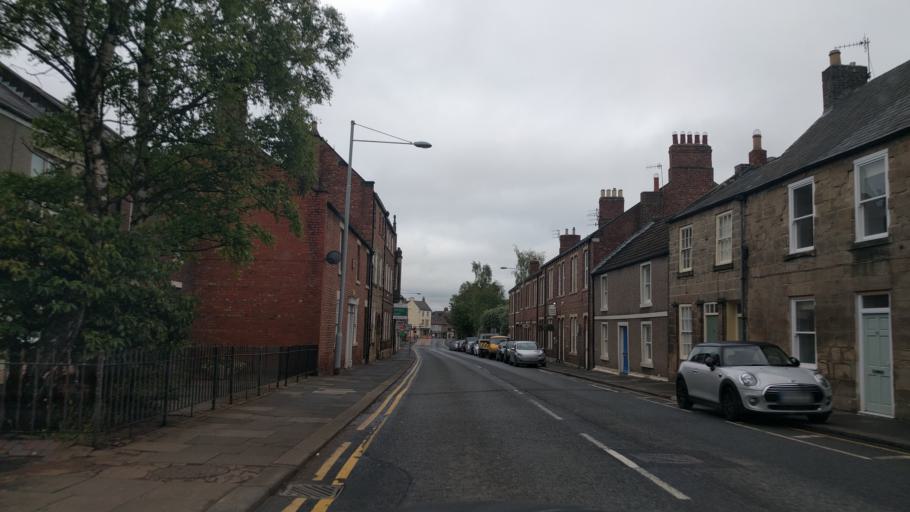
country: GB
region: England
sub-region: Northumberland
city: Morpeth
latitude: 55.1707
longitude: -1.6938
